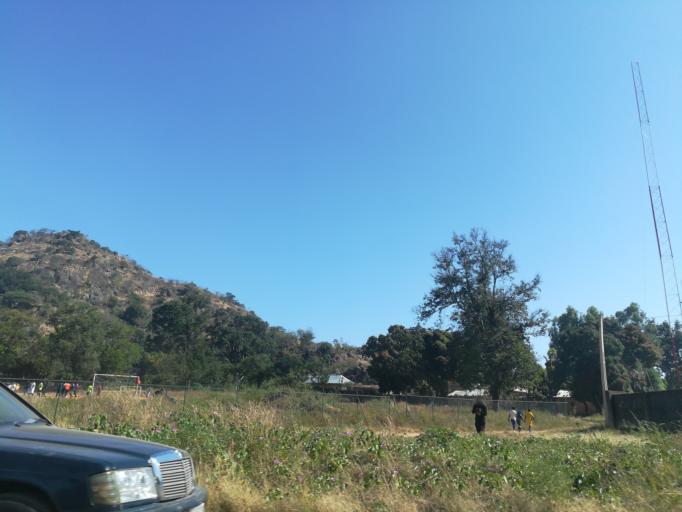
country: NG
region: Plateau
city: Jos
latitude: 9.9372
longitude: 8.9023
